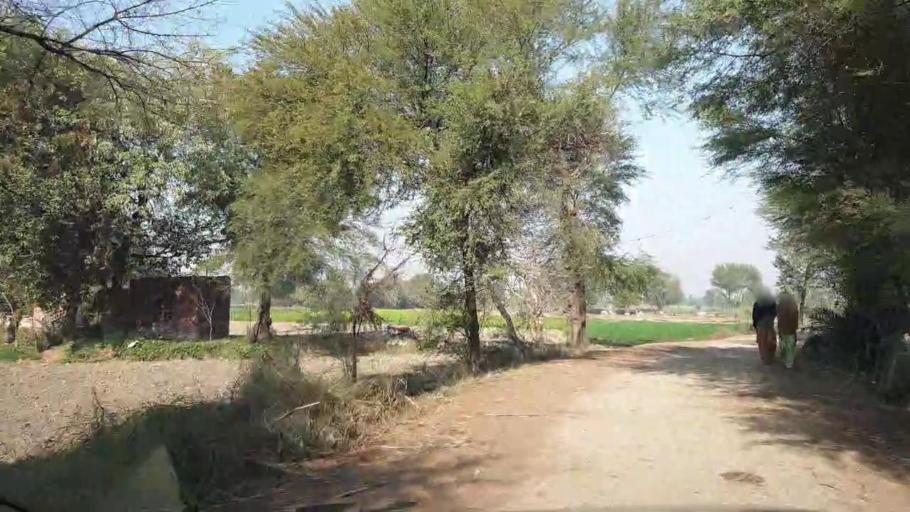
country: PK
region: Sindh
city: Ubauro
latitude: 28.1113
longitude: 69.7738
